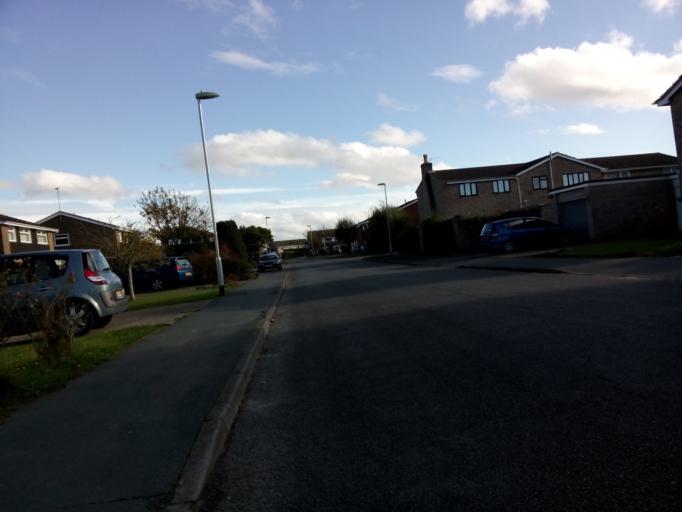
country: GB
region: England
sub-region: Suffolk
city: Kesgrave
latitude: 52.0510
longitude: 1.2060
